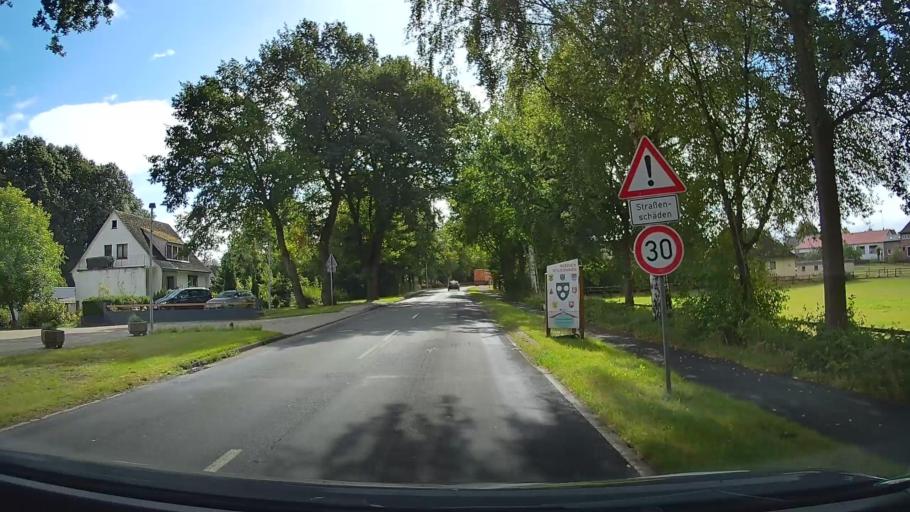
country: DE
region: Lower Saxony
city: Rhade
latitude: 53.3301
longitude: 9.1142
